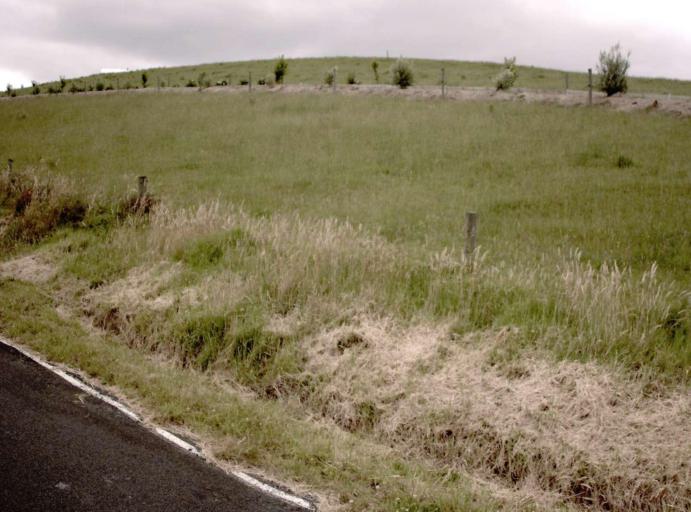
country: AU
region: Victoria
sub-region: Latrobe
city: Traralgon
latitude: -38.4840
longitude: 146.6271
